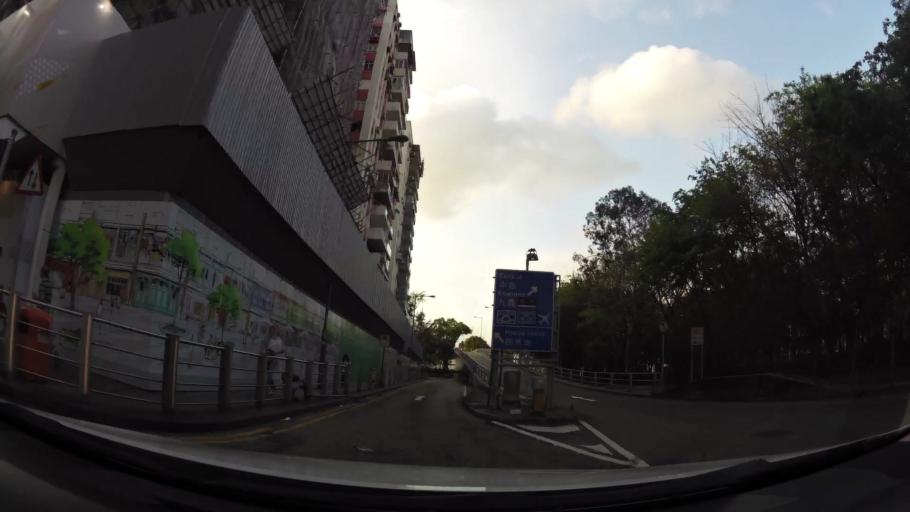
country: HK
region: Wanchai
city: Wan Chai
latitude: 22.2820
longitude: 114.1865
